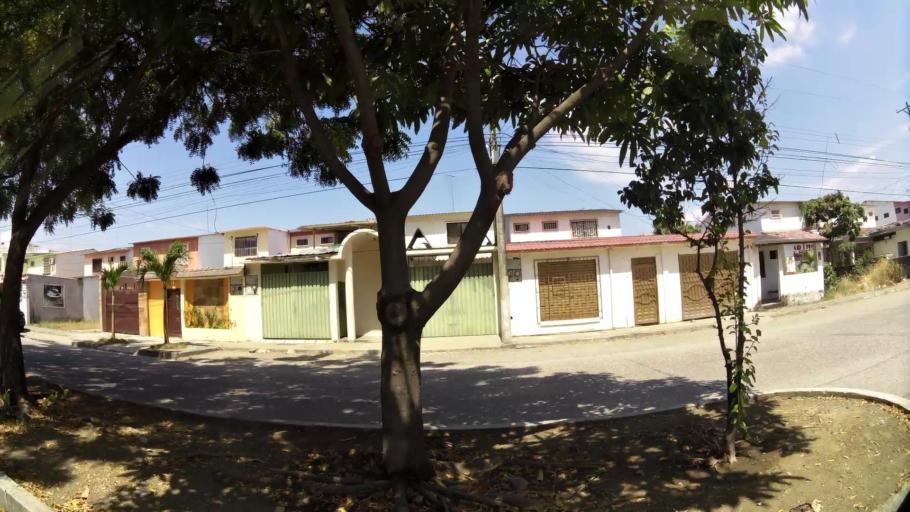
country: EC
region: Guayas
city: Eloy Alfaro
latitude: -2.1107
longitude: -79.9046
